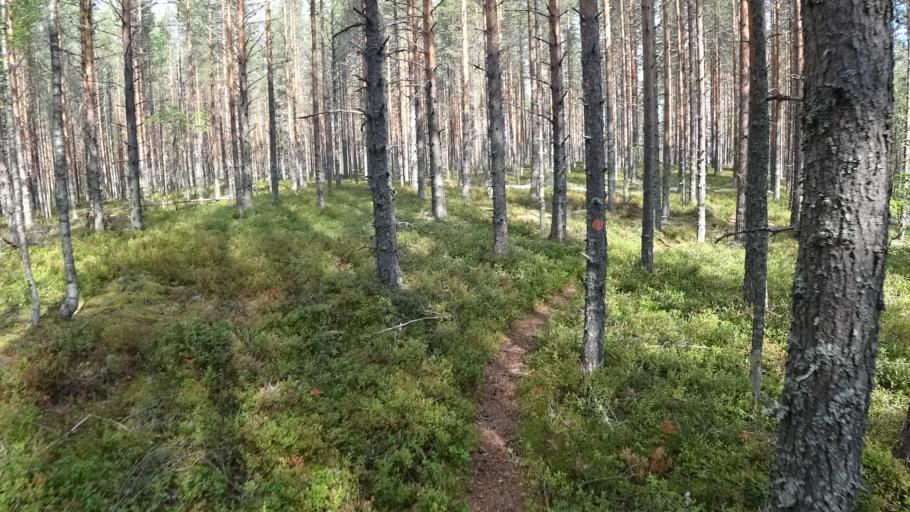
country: FI
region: North Karelia
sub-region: Joensuu
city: Ilomantsi
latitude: 62.6058
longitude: 31.1882
